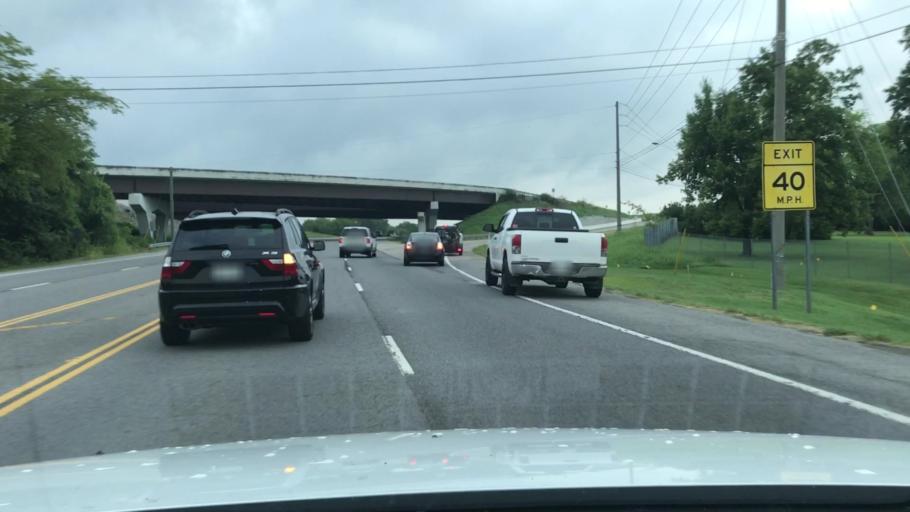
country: US
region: Tennessee
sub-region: Sumner County
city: Hendersonville
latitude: 36.3276
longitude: -86.5605
